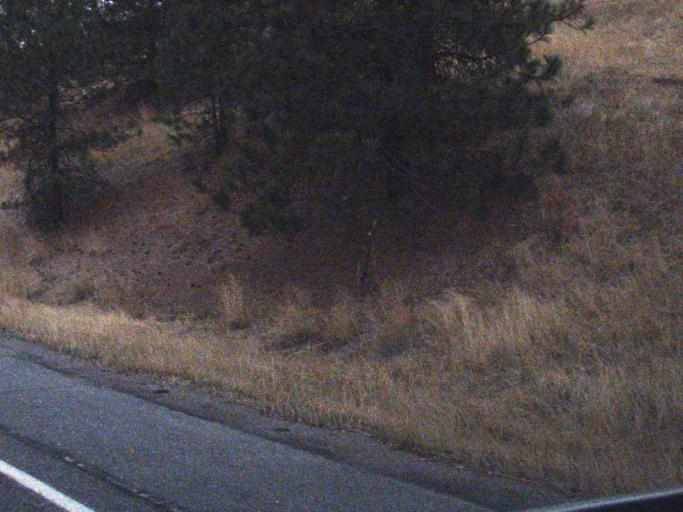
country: US
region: Washington
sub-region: Stevens County
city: Kettle Falls
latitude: 48.5934
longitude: -117.9989
